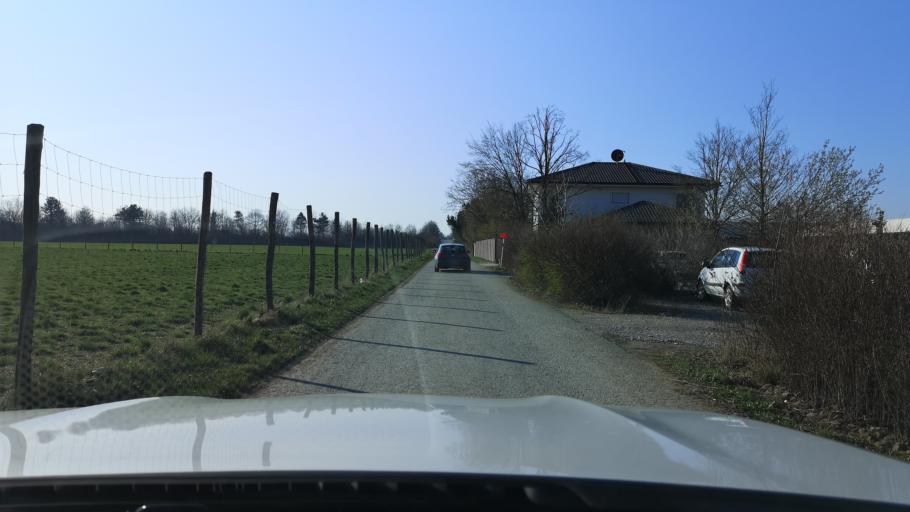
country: DE
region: Bavaria
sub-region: Upper Bavaria
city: Poing
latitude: 48.1552
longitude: 11.8114
